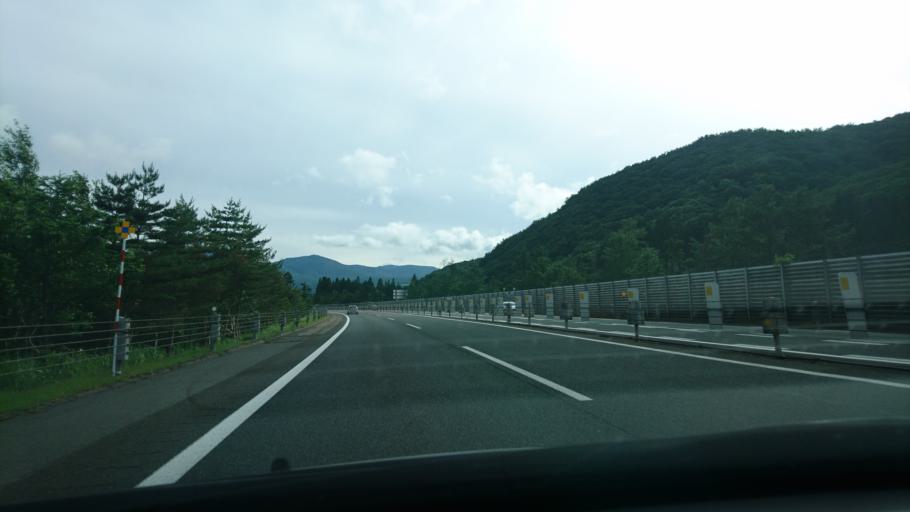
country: JP
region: Akita
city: Hanawa
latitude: 40.0429
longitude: 140.9936
